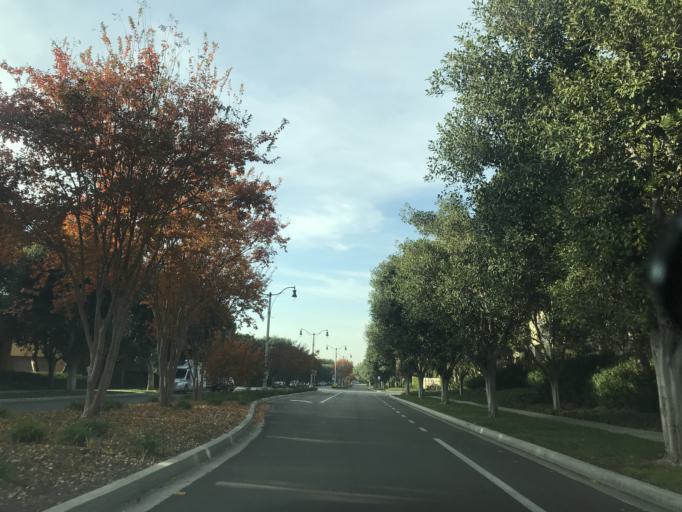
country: US
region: California
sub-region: Orange County
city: North Tustin
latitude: 33.7012
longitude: -117.7469
